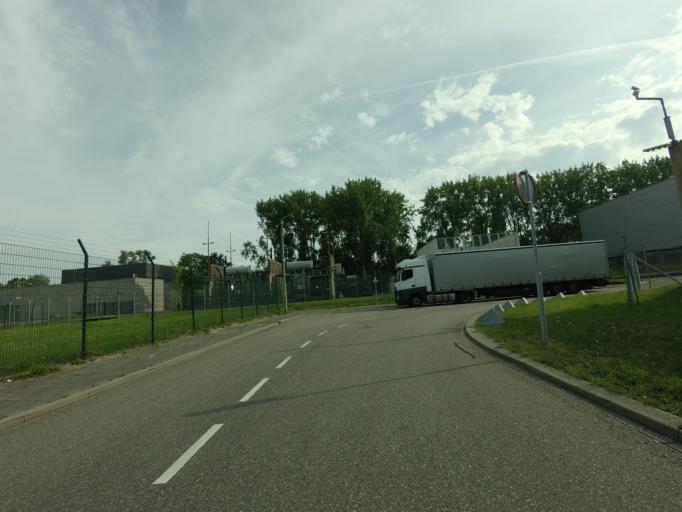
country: NL
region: South Holland
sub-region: Gemeente Papendrecht
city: Papendrecht
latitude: 51.8180
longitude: 4.7125
